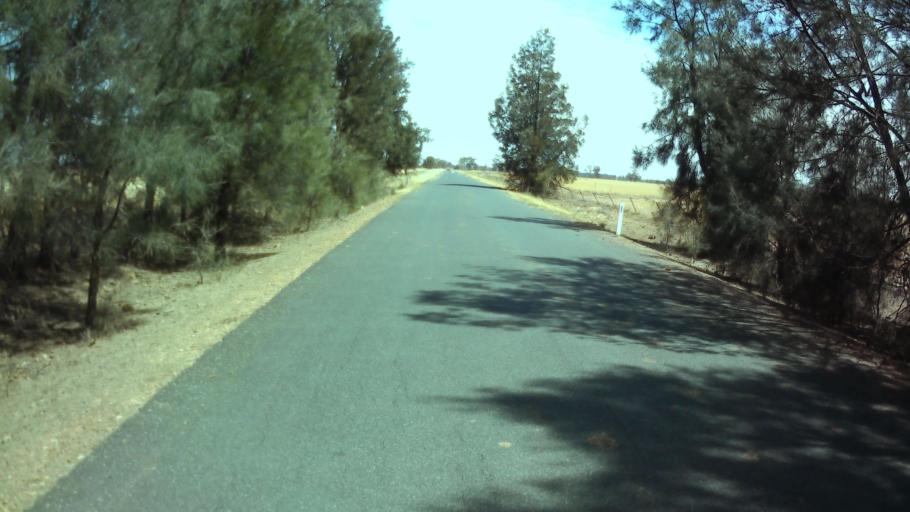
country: AU
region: New South Wales
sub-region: Weddin
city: Grenfell
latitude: -33.9299
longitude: 147.7625
